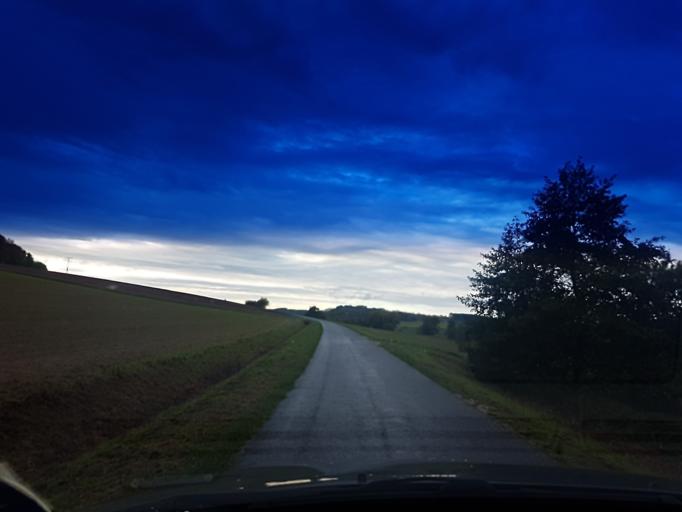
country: DE
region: Bavaria
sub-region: Upper Franconia
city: Schlusselfeld
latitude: 49.7606
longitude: 10.5987
